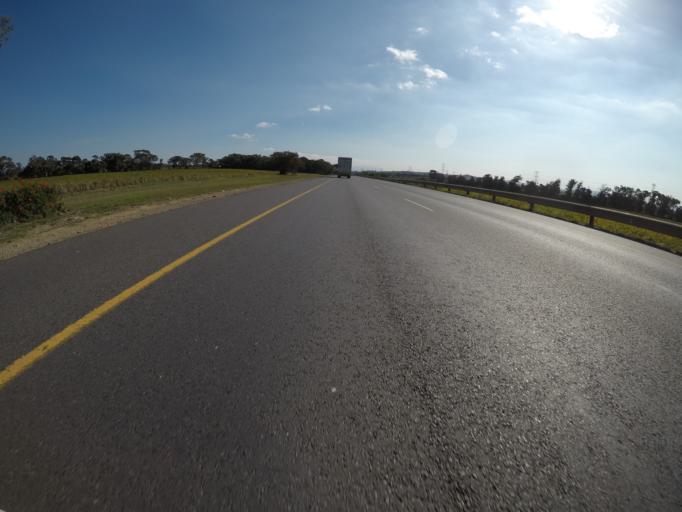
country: ZA
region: Western Cape
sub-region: City of Cape Town
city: Kraaifontein
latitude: -33.8817
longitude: 18.7592
